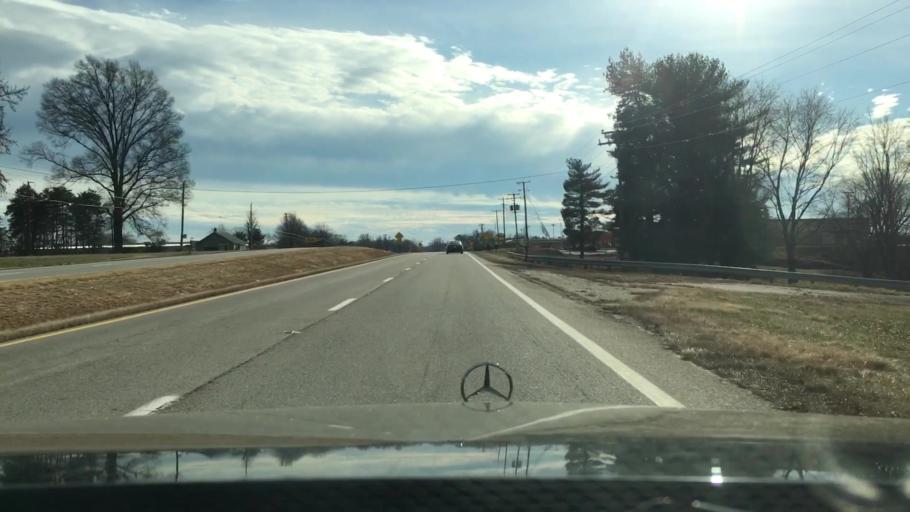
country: US
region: Virginia
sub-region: Pittsylvania County
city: Mount Hermon
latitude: 36.7364
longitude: -79.3808
